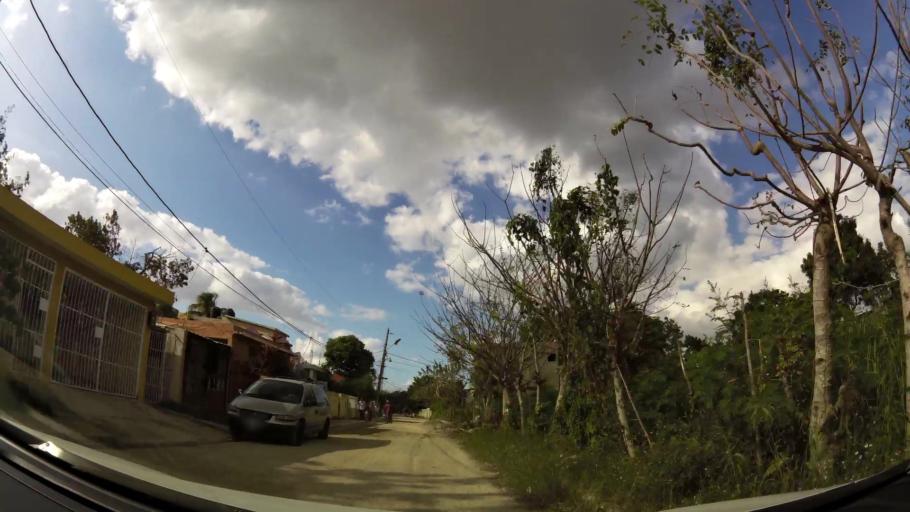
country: DO
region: Nacional
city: Ensanche Luperon
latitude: 18.5576
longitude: -69.9009
